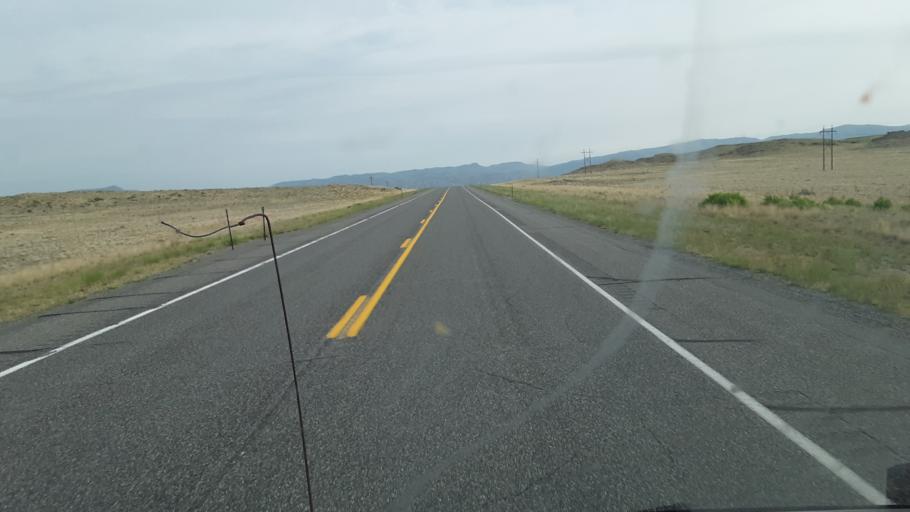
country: US
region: Wyoming
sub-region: Hot Springs County
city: Thermopolis
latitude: 43.3018
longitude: -108.1282
